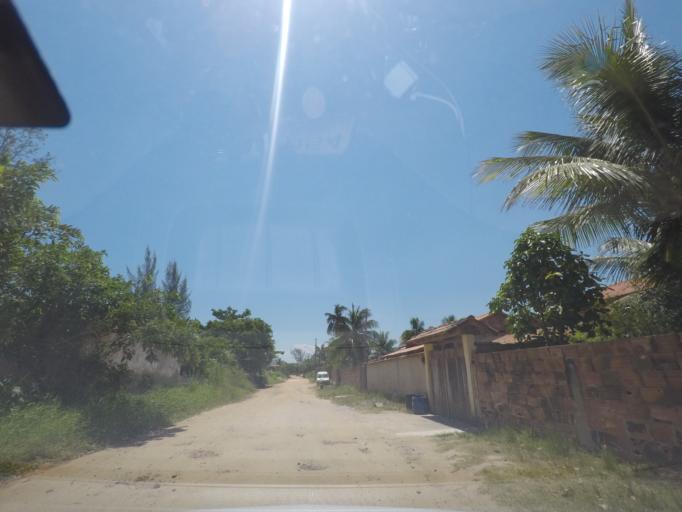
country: BR
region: Rio de Janeiro
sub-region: Marica
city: Marica
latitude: -22.9708
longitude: -42.9396
